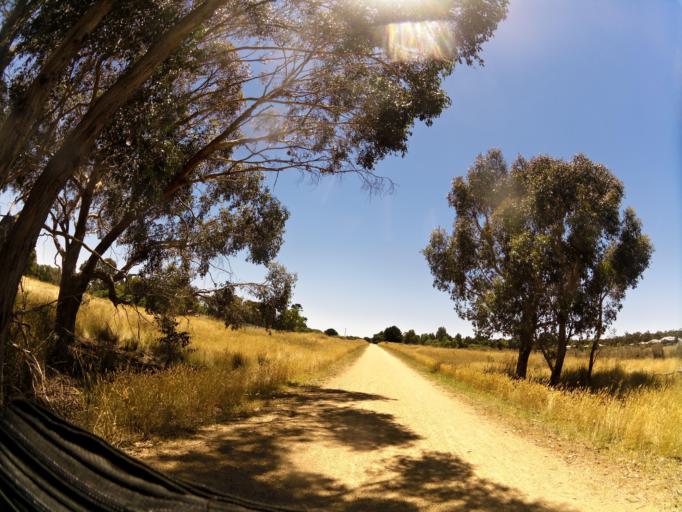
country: AU
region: Victoria
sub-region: Ballarat North
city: Delacombe
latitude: -37.5963
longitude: 143.7195
